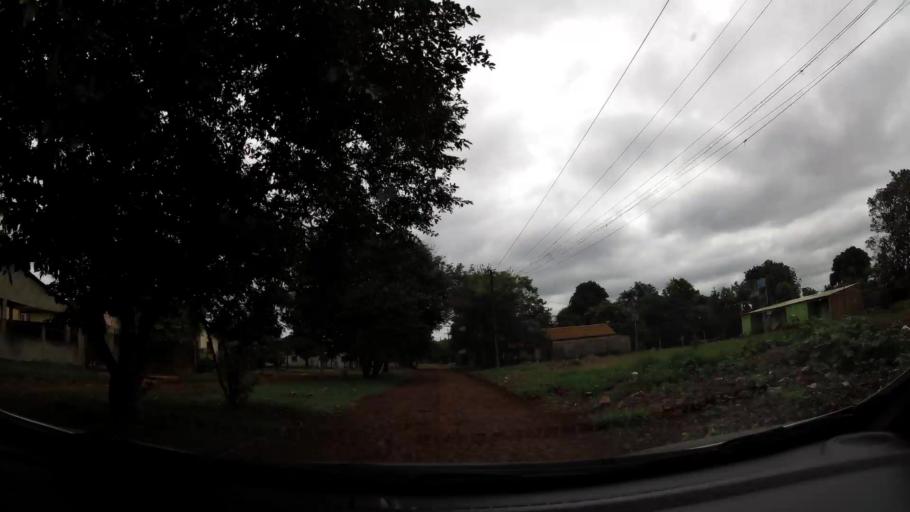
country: PY
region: Alto Parana
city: Ciudad del Este
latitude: -25.3763
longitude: -54.6528
